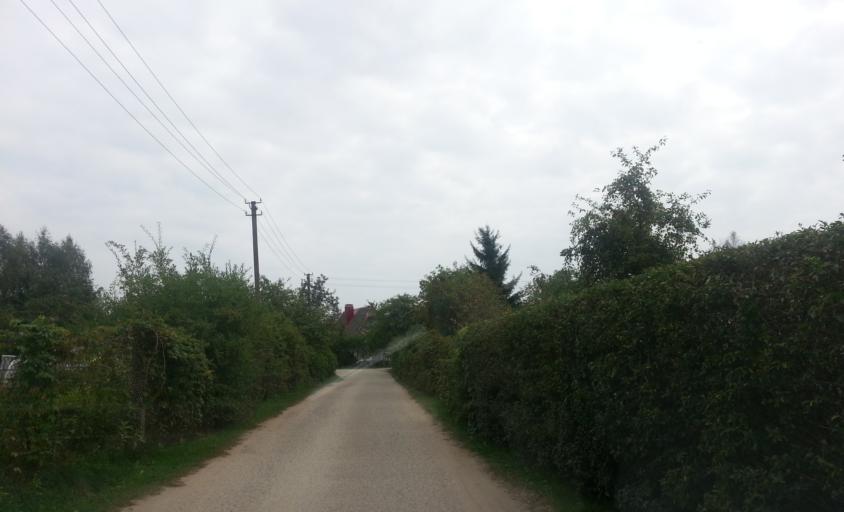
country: LT
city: Grigiskes
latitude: 54.7551
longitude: 25.0174
